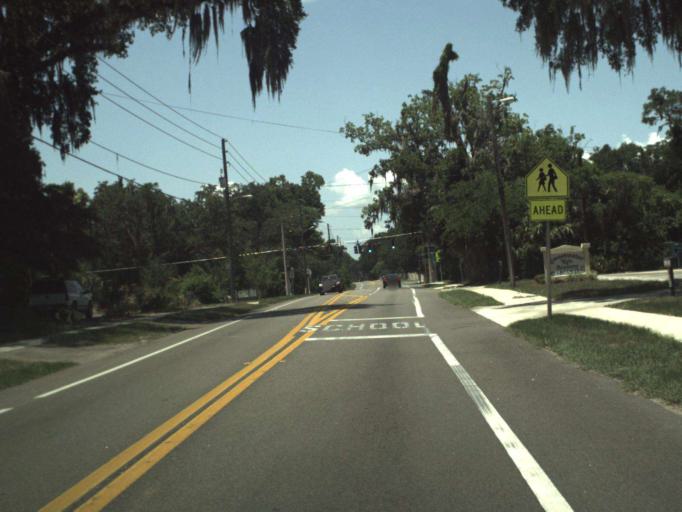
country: US
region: Florida
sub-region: Seminole County
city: Oviedo
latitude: 28.6759
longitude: -81.2084
